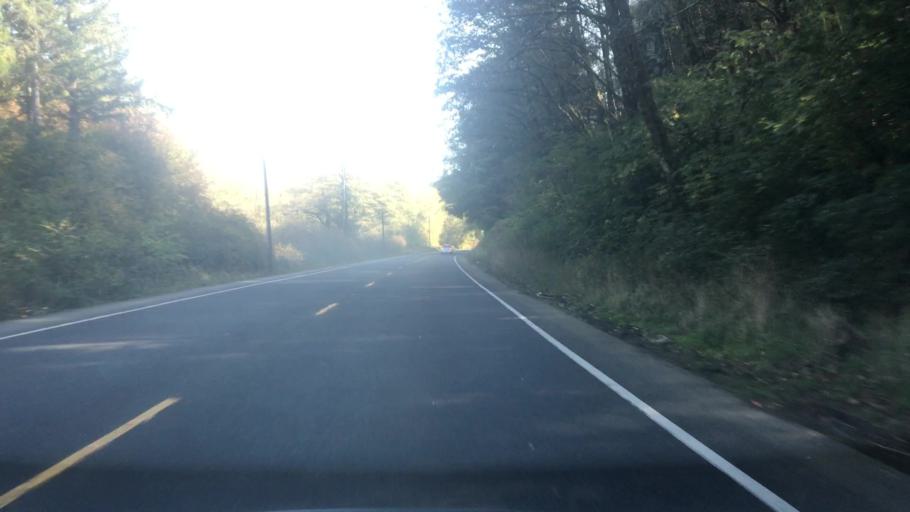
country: US
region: Oregon
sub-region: Lincoln County
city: Rose Lodge
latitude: 45.0109
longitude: -123.9241
